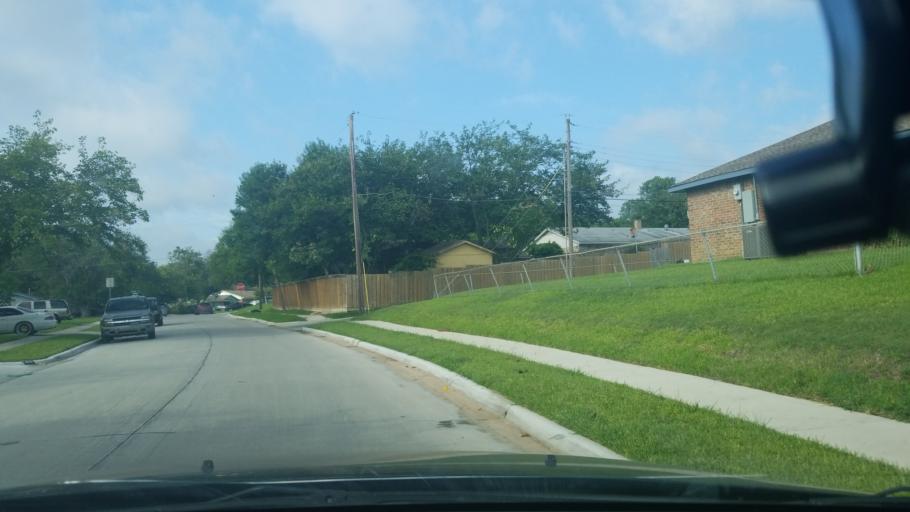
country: US
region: Texas
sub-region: Dallas County
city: Mesquite
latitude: 32.7724
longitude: -96.6375
